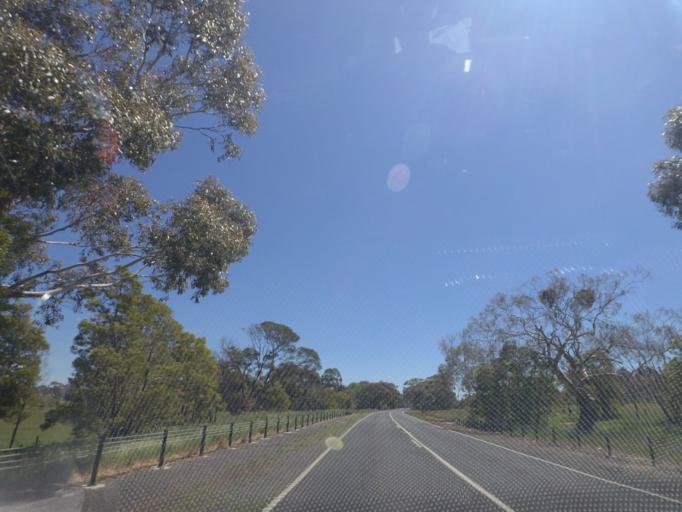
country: AU
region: Victoria
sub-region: Melton
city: Melton West
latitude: -37.5325
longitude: 144.5686
